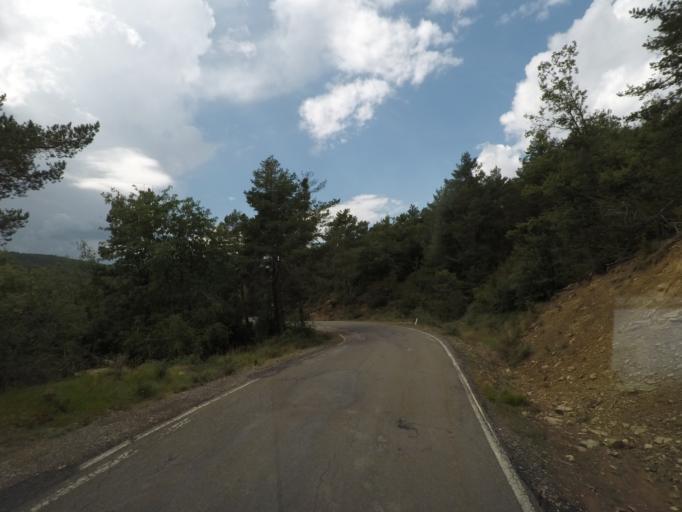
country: ES
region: Aragon
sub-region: Provincia de Huesca
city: Boltana
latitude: 42.3981
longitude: -0.0389
